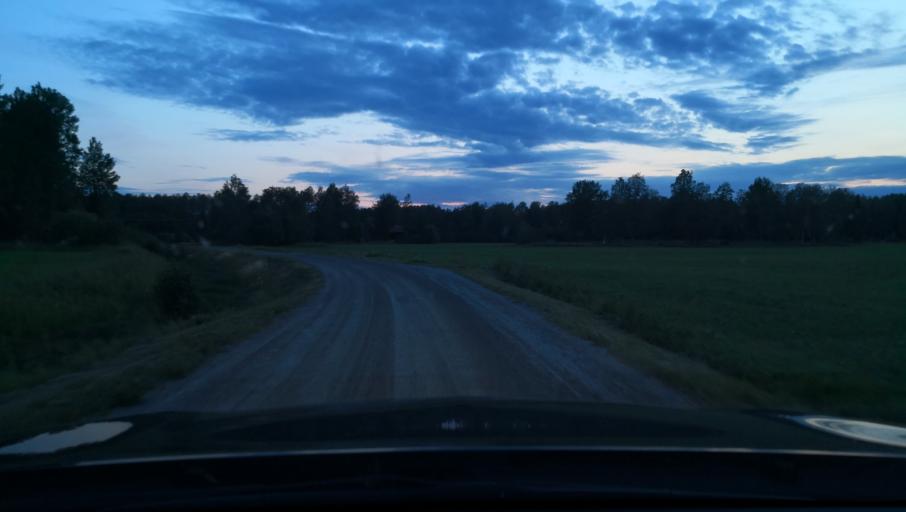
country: SE
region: Uppsala
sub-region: Heby Kommun
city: OEstervala
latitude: 60.0148
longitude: 17.3010
